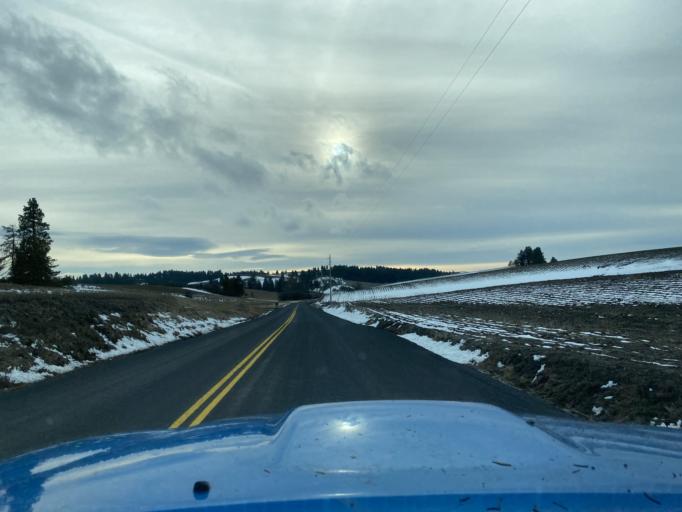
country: US
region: Idaho
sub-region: Latah County
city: Moscow
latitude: 46.6922
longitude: -116.8704
